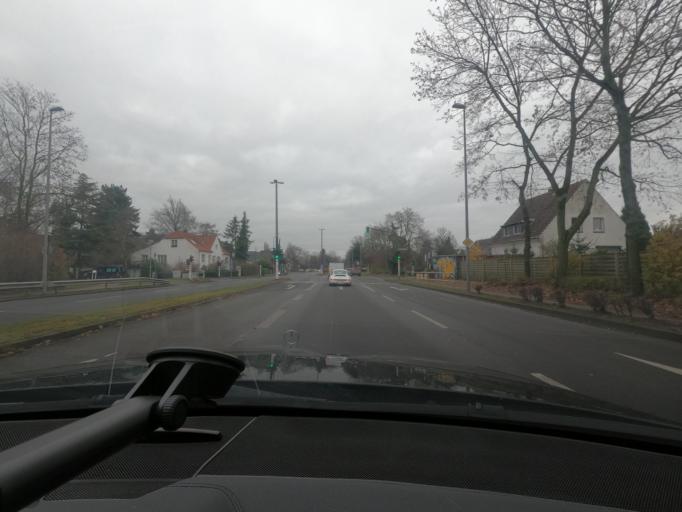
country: DE
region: North Rhine-Westphalia
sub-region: Regierungsbezirk Dusseldorf
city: Krefeld
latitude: 51.3514
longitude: 6.5669
